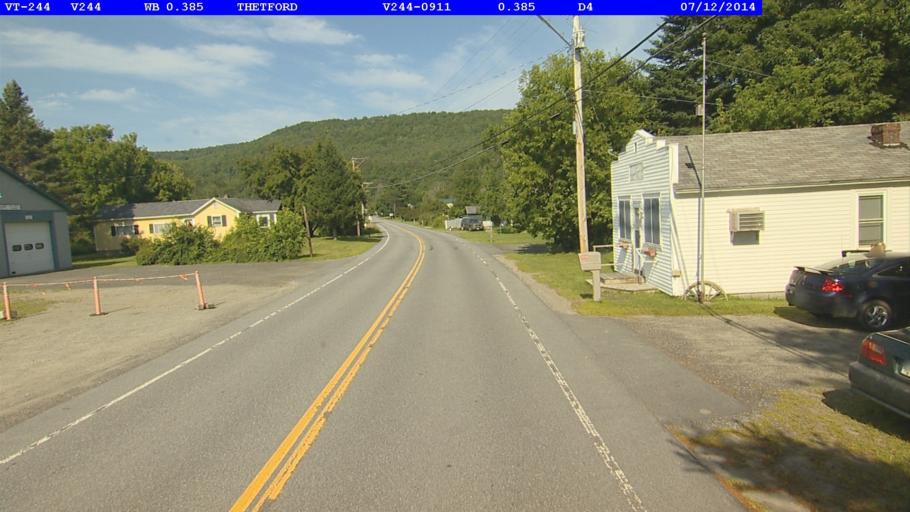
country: US
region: New Hampshire
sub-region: Grafton County
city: Orford
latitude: 43.8872
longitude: -72.2531
